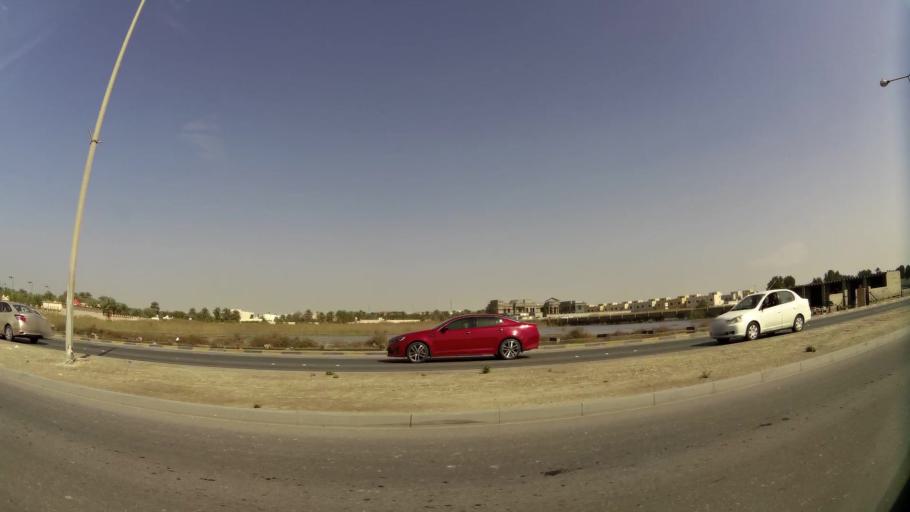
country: BH
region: Central Governorate
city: Madinat Hamad
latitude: 26.1836
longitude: 50.4657
